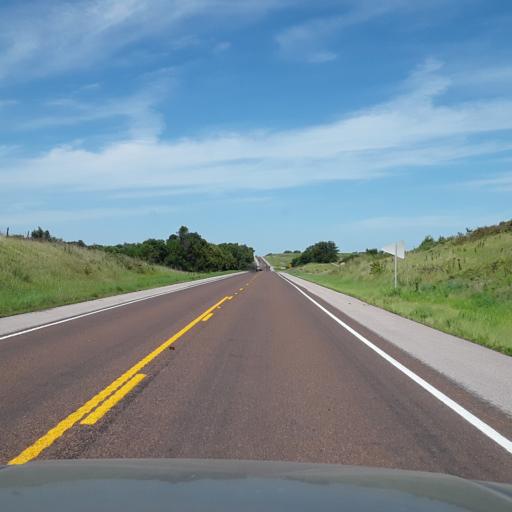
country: US
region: Nebraska
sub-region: Lancaster County
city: Lincoln
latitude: 40.8866
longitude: -96.8650
